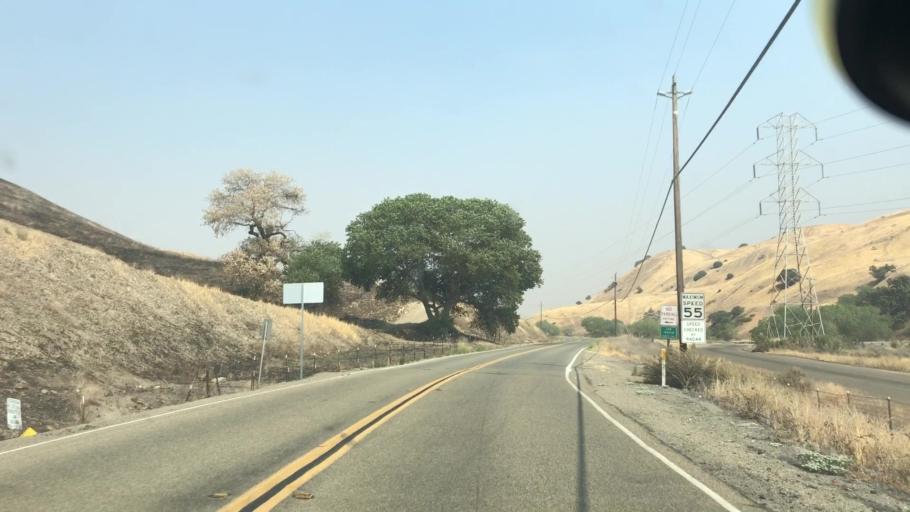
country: US
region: California
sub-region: San Joaquin County
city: Mountain House
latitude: 37.6362
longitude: -121.5574
